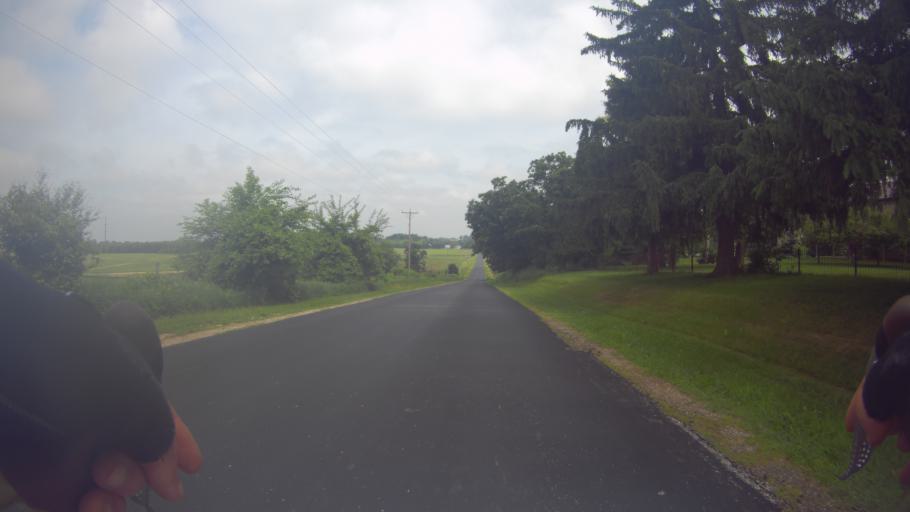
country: US
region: Wisconsin
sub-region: Rock County
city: Edgerton
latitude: 42.9118
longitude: -89.0427
